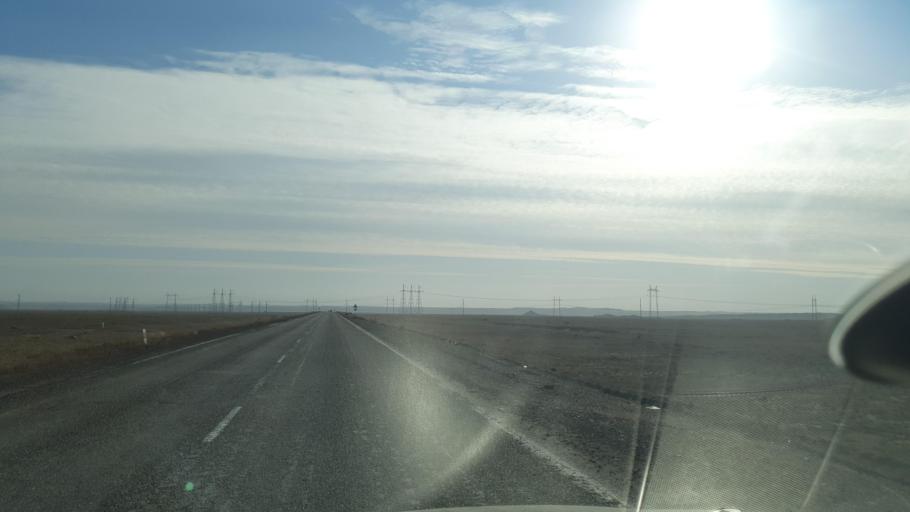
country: KZ
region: Zhambyl
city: Mynaral
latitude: 45.6080
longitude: 73.3968
